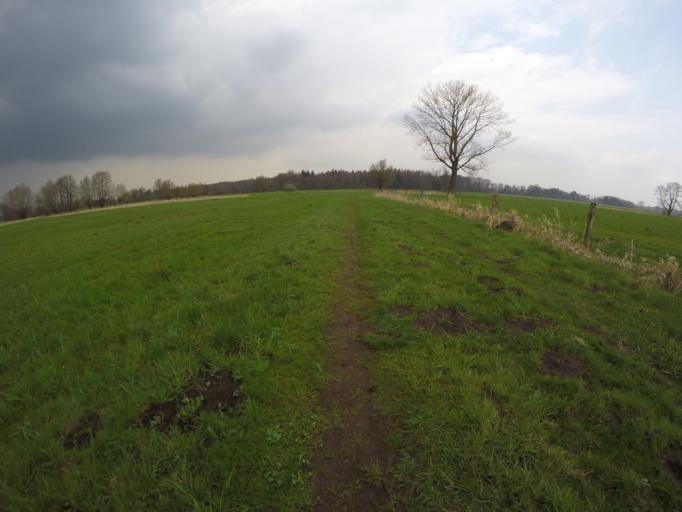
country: DE
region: Schleswig-Holstein
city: Borstel-Hohenraden
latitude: 53.7259
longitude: 9.8125
